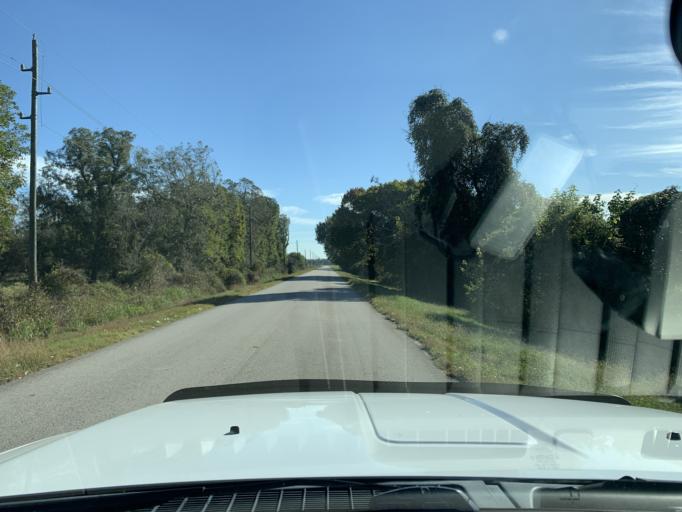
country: US
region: Texas
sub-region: Fort Bend County
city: Rosenberg
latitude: 29.6213
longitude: -95.8214
